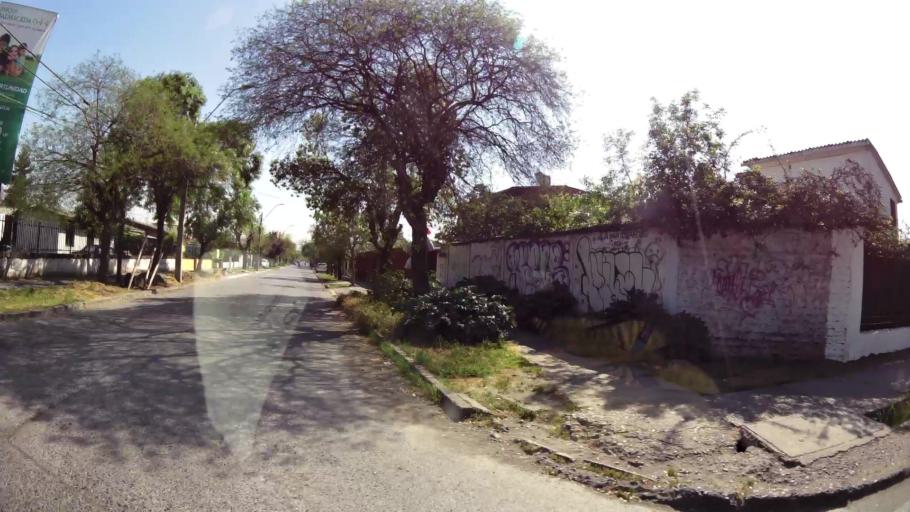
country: CL
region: Santiago Metropolitan
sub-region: Provincia de Maipo
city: San Bernardo
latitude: -33.5917
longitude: -70.6962
